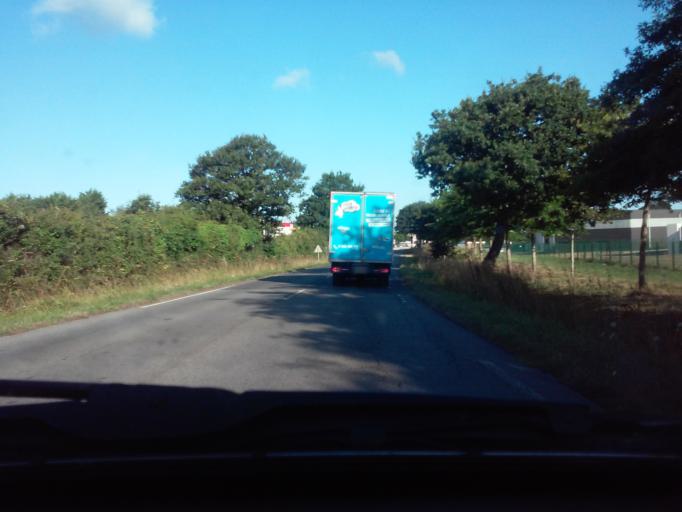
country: FR
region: Pays de la Loire
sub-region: Departement de la Loire-Atlantique
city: Saint-Andre-des-Eaux
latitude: 47.2953
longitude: -2.2891
